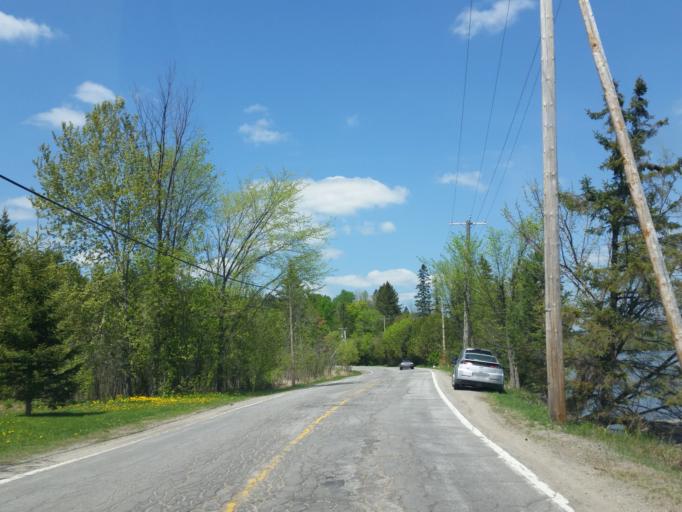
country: CA
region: Quebec
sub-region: Outaouais
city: Wakefield
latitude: 45.6074
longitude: -75.8940
